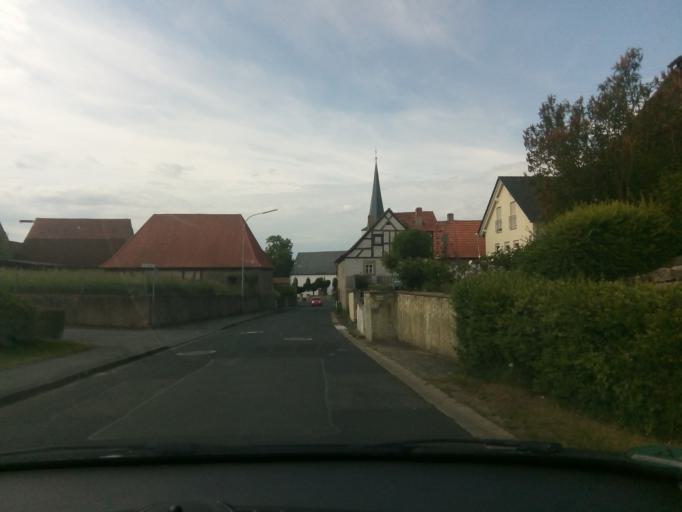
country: DE
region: Bavaria
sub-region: Regierungsbezirk Unterfranken
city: Volkach
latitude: 49.8724
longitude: 10.2595
